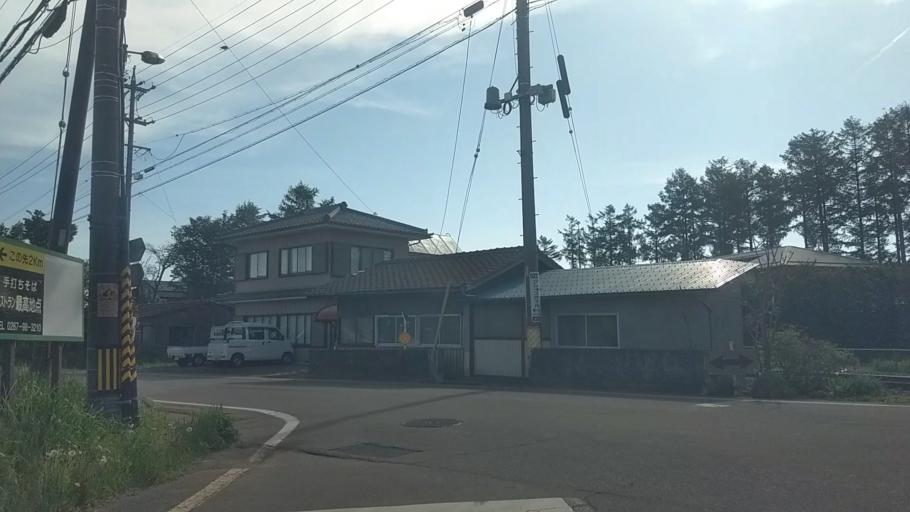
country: JP
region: Yamanashi
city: Nirasaki
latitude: 35.9516
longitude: 138.4724
